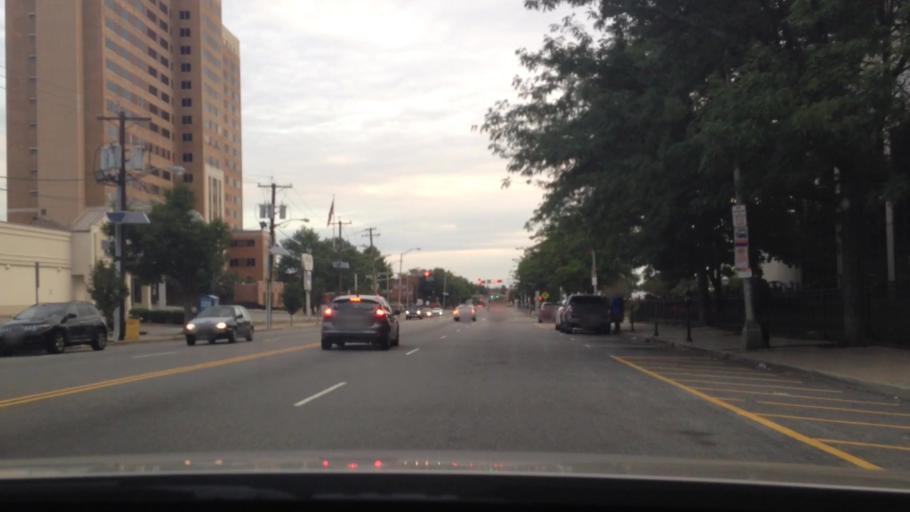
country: US
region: New Jersey
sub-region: Essex County
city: Newark
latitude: 40.7414
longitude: -74.1918
